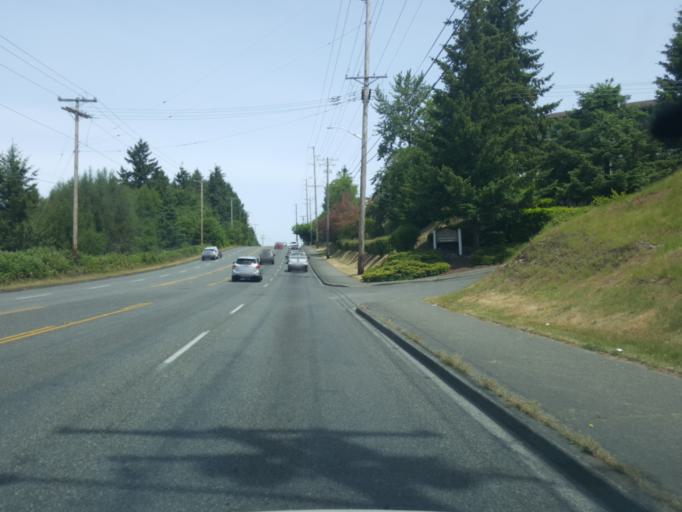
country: US
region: Washington
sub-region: Pierce County
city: Fircrest
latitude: 47.2248
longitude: -122.5051
